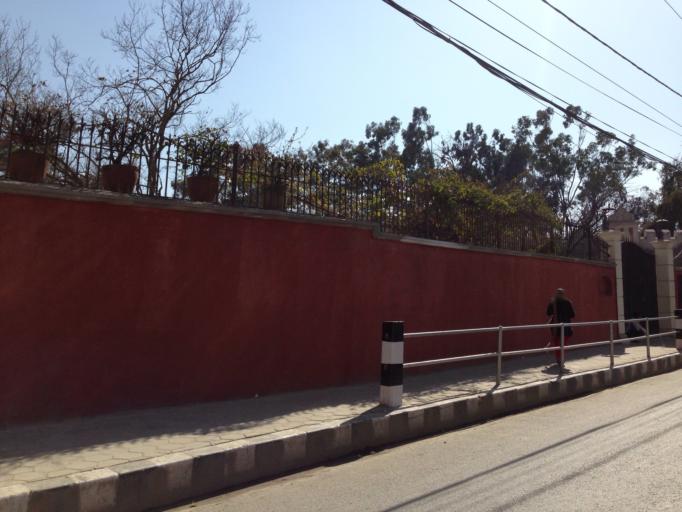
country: NP
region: Central Region
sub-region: Bagmati Zone
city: Kathmandu
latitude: 27.7351
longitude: 85.3313
